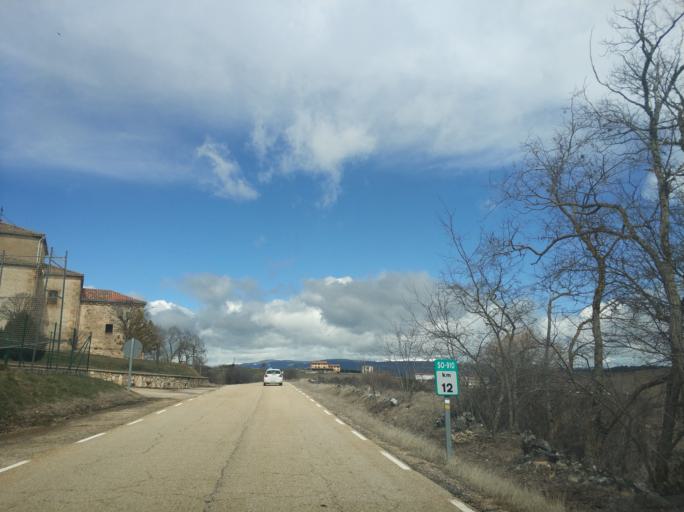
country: ES
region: Castille and Leon
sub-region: Provincia de Soria
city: Abejar
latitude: 41.8033
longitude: -2.7811
